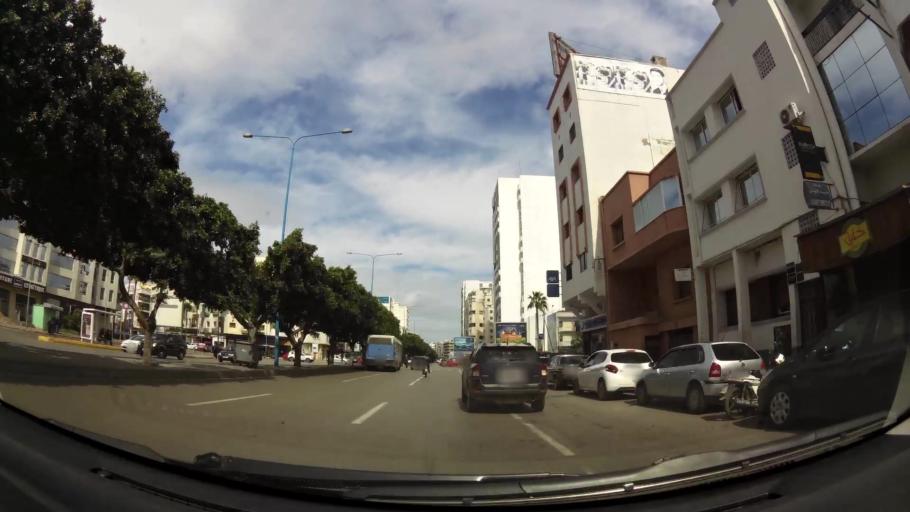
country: MA
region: Grand Casablanca
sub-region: Casablanca
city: Casablanca
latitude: 33.5825
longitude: -7.6402
